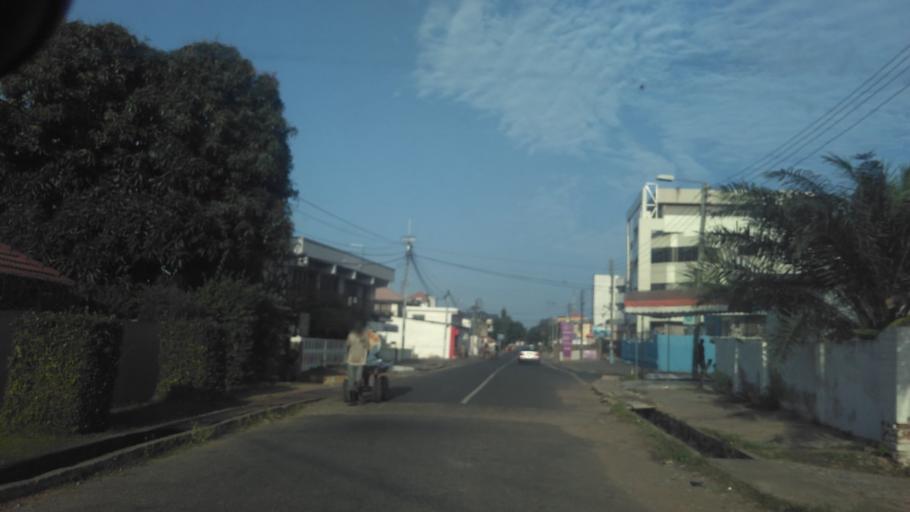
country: GH
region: Greater Accra
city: Accra
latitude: 5.5715
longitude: -0.2046
